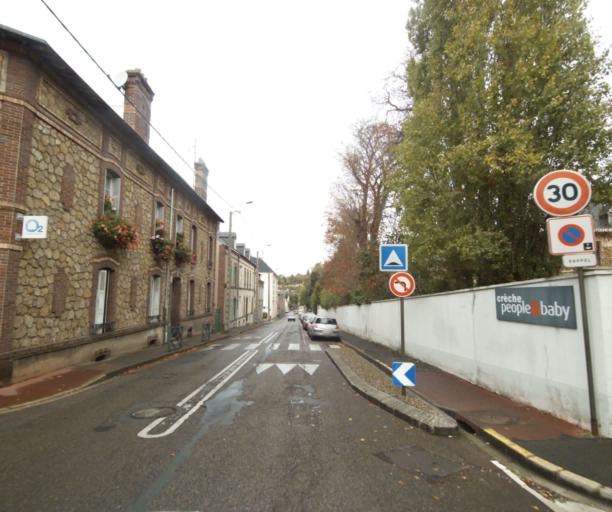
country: FR
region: Centre
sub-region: Departement d'Eure-et-Loir
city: Dreux
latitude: 48.7343
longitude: 1.3731
